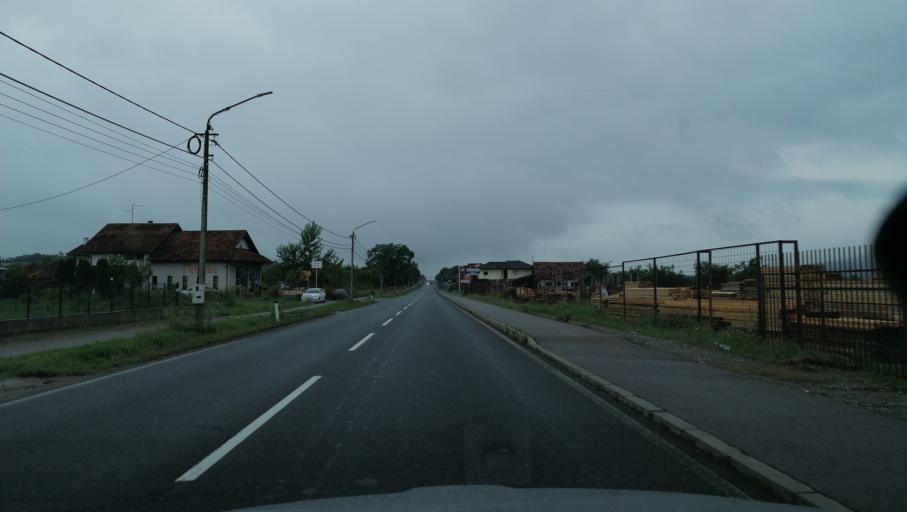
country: RS
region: Central Serbia
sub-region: Rasinski Okrug
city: Krusevac
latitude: 43.5871
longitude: 21.2787
